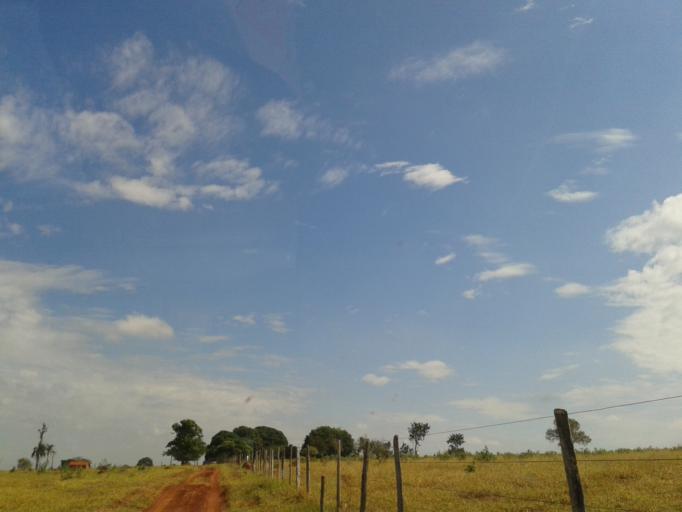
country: BR
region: Minas Gerais
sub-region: Campina Verde
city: Campina Verde
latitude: -19.3771
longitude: -49.6711
